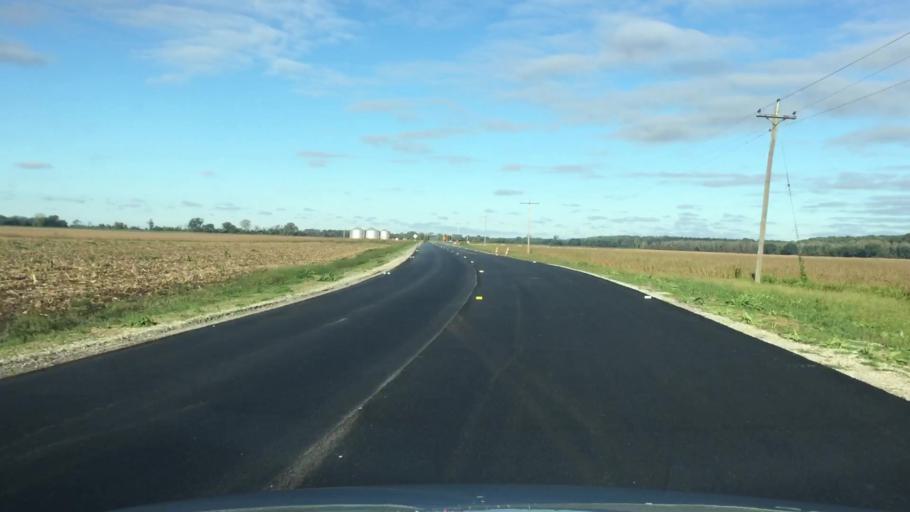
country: US
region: Missouri
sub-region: Howard County
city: New Franklin
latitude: 38.9999
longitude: -92.6751
